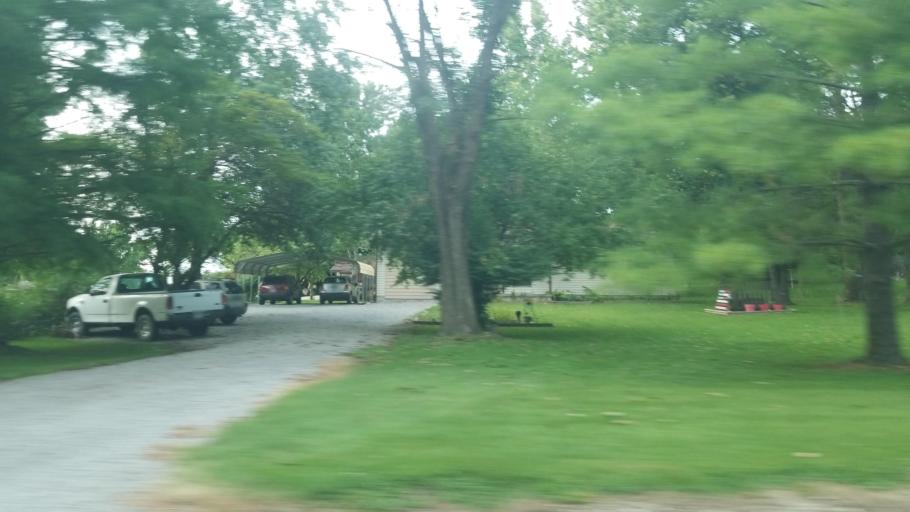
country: US
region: Illinois
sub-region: Saline County
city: Harrisburg
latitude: 37.8478
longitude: -88.6129
